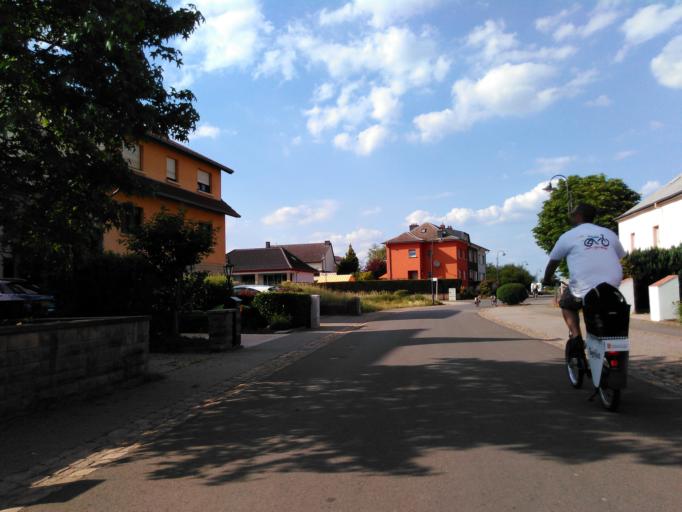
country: LU
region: Luxembourg
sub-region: Canton d'Esch-sur-Alzette
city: Kayl
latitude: 49.4902
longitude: 6.0412
